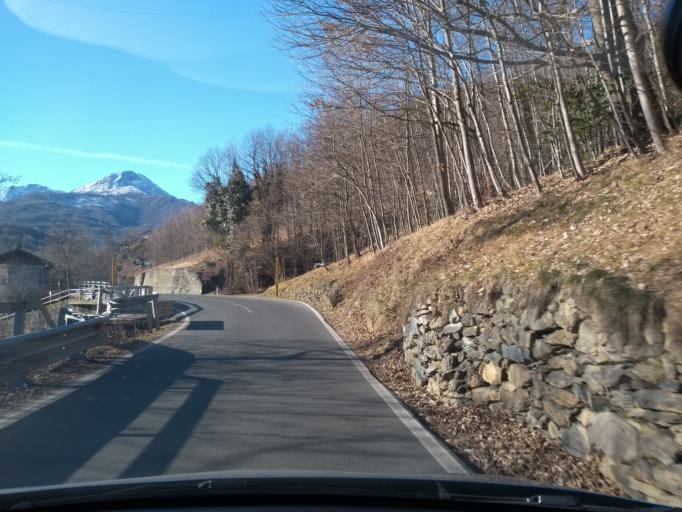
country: IT
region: Piedmont
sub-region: Provincia di Torino
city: Viu
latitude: 45.2383
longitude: 7.3986
